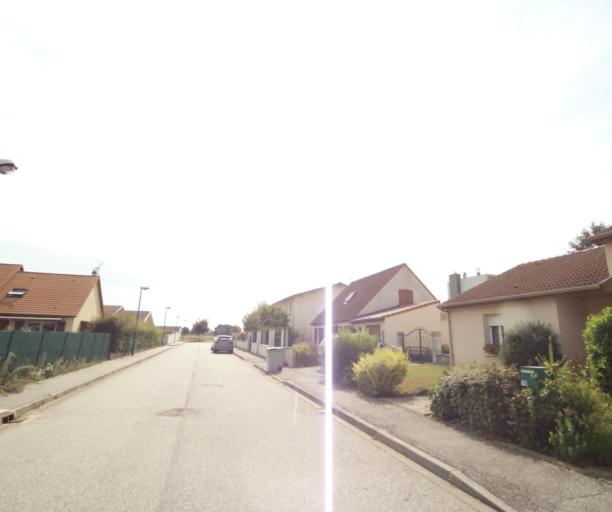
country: FR
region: Lorraine
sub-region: Departement de Meurthe-et-Moselle
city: Luneville
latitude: 48.5938
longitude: 6.5113
